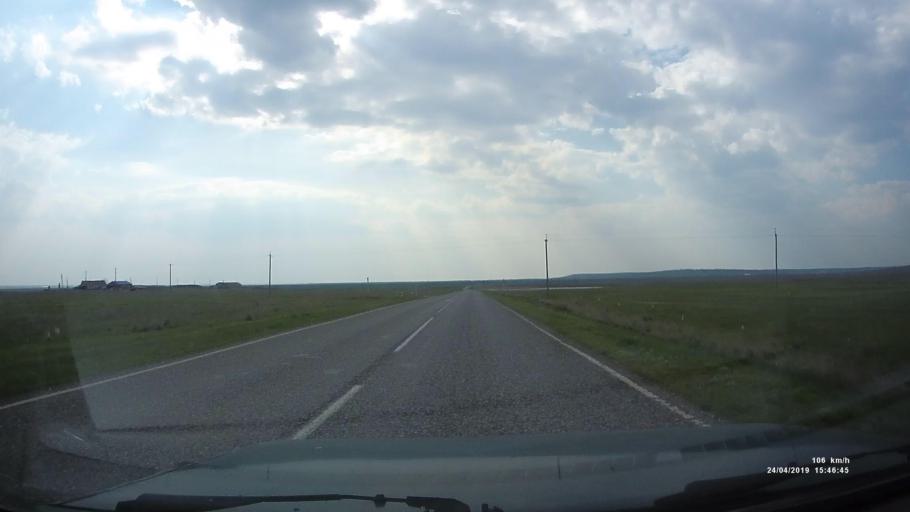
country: RU
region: Kalmykiya
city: Yashalta
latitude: 46.5933
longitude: 42.7074
